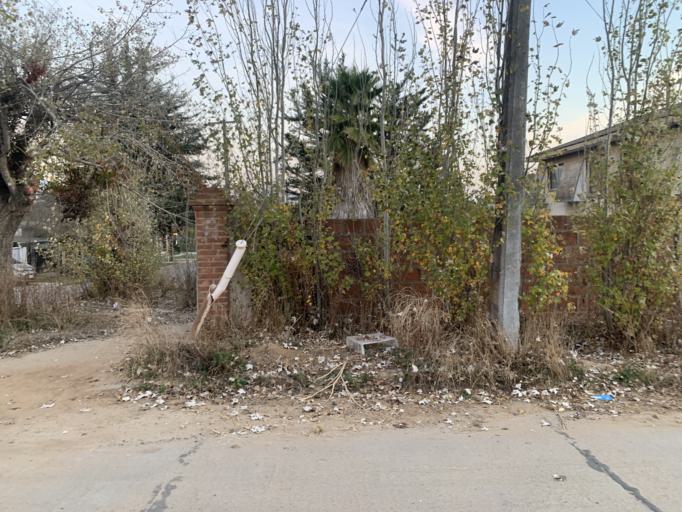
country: CL
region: Valparaiso
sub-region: Provincia de Marga Marga
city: Villa Alemana
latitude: -33.0384
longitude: -71.3530
